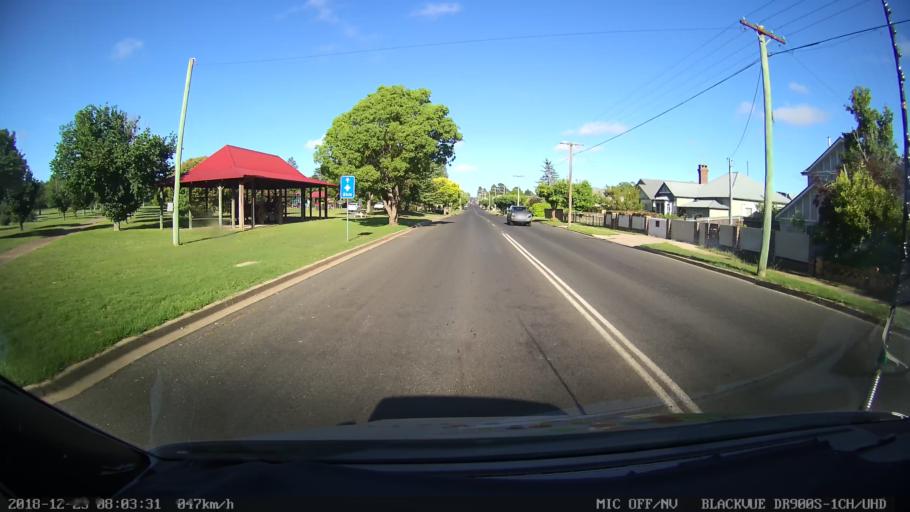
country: AU
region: New South Wales
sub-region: Armidale Dumaresq
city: Armidale
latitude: -30.5191
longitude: 151.6724
